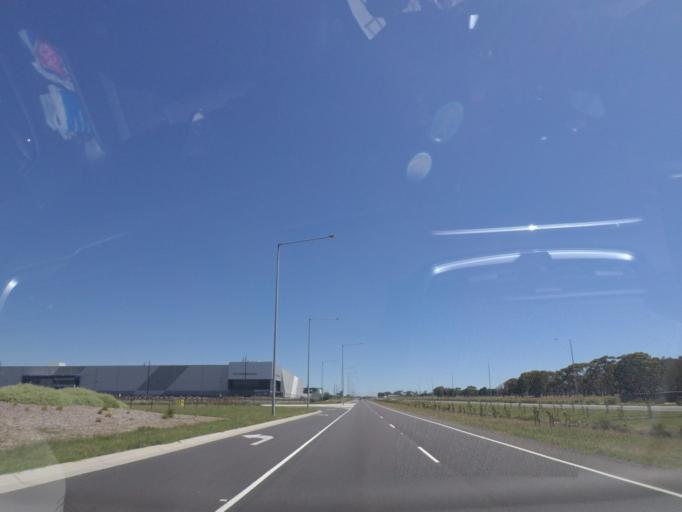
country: AU
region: Victoria
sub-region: Hume
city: Tullamarine
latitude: -37.6979
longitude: 144.8668
